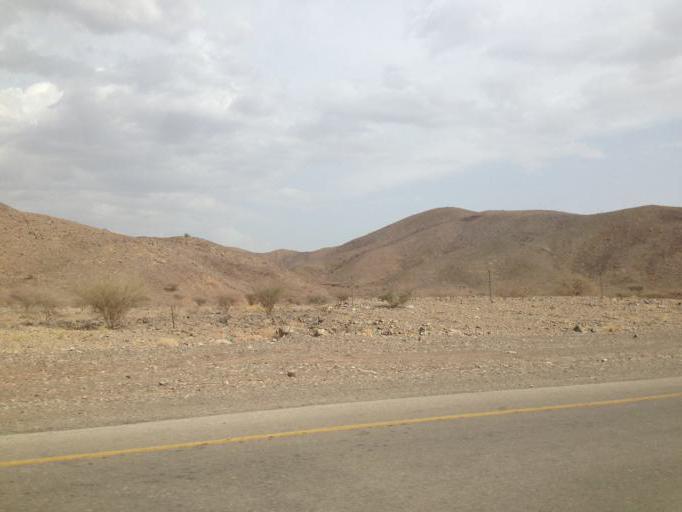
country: OM
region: Ash Sharqiyah
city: Badiyah
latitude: 22.5286
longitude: 58.9548
